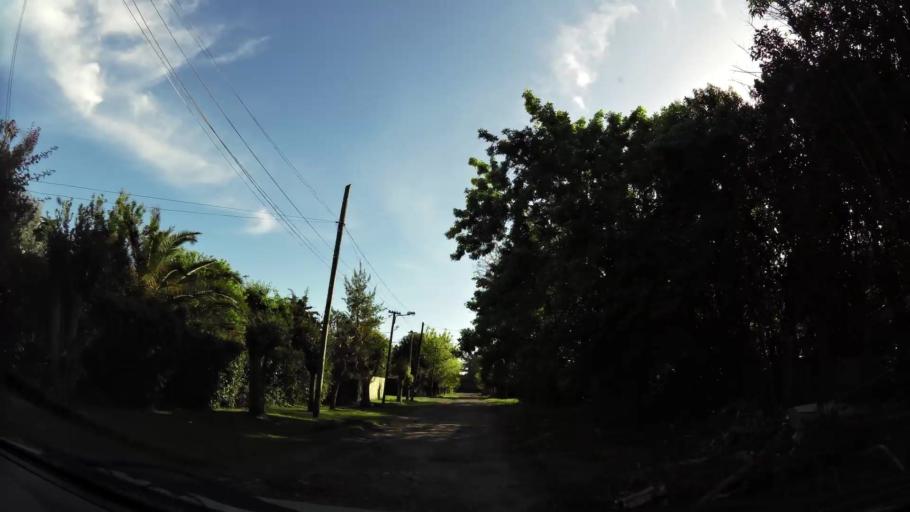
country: AR
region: Buenos Aires
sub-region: Partido de Quilmes
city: Quilmes
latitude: -34.8151
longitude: -58.2157
